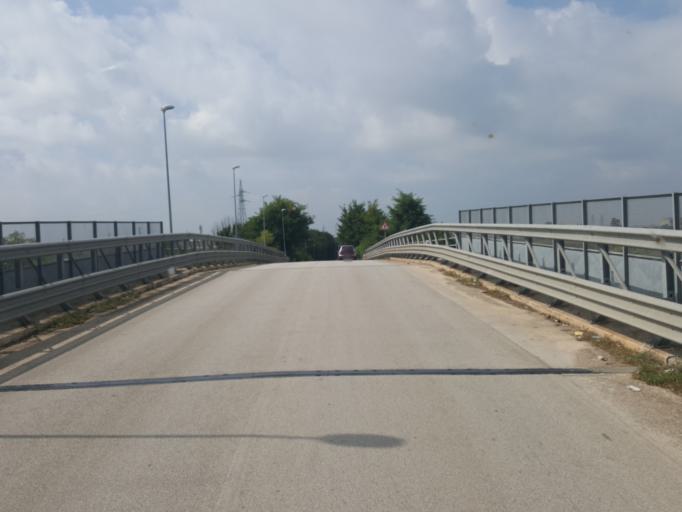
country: IT
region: Campania
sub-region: Provincia di Caserta
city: Pignataro Maggiore
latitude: 41.1792
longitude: 14.1549
